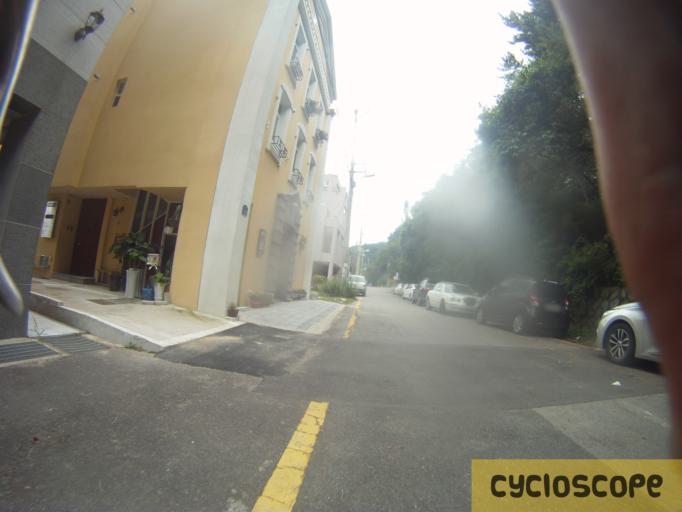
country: KR
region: Busan
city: Kijang
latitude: 35.1748
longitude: 129.1953
